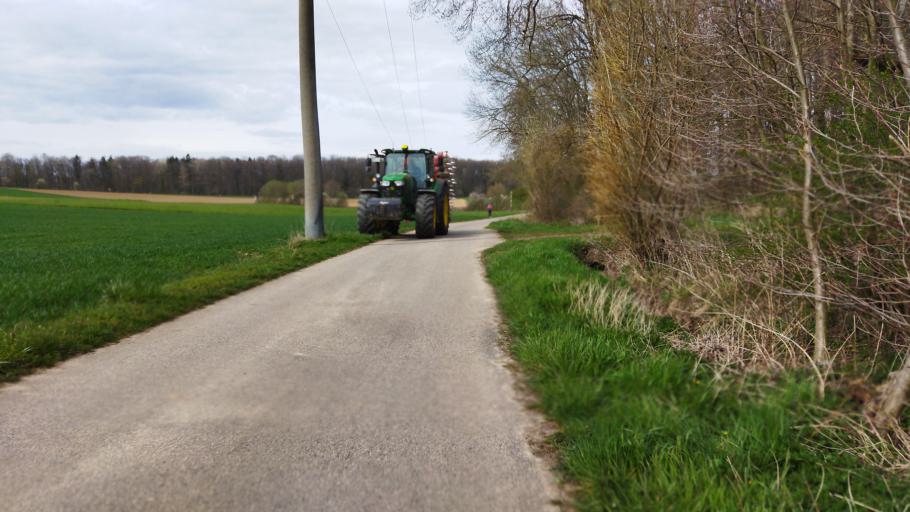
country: DE
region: Baden-Wuerttemberg
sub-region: Regierungsbezirk Stuttgart
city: Gundelsheim
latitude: 49.2891
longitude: 9.1851
